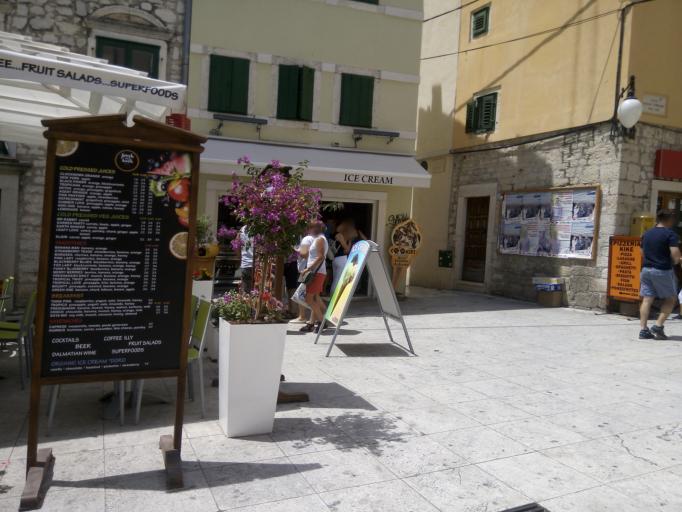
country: HR
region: Sibensko-Kniniska
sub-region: Grad Sibenik
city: Sibenik
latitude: 43.7349
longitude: 15.8930
